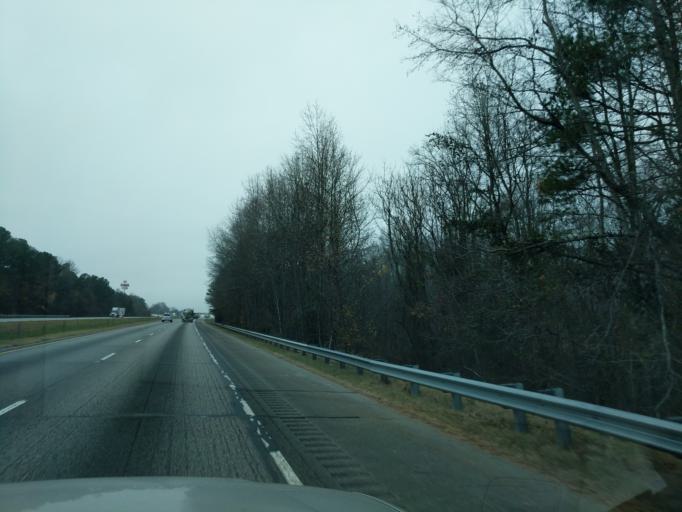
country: US
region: Georgia
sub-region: Franklin County
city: Carnesville
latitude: 34.3963
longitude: -83.2181
